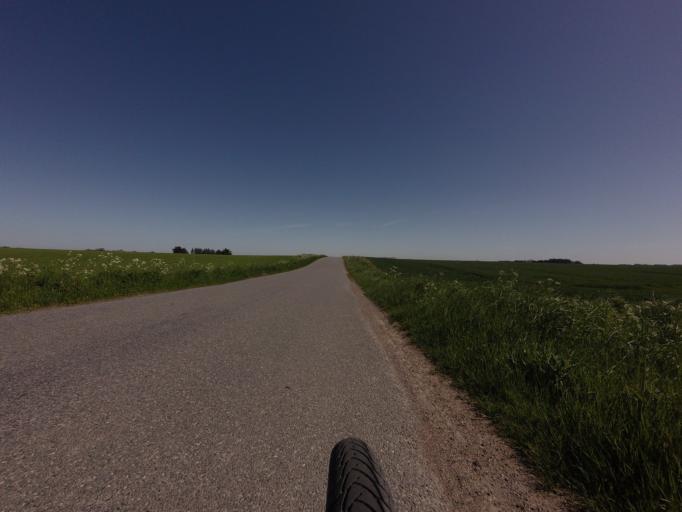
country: DK
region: North Denmark
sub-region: Hjorring Kommune
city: Vra
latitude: 57.4112
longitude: 9.8734
